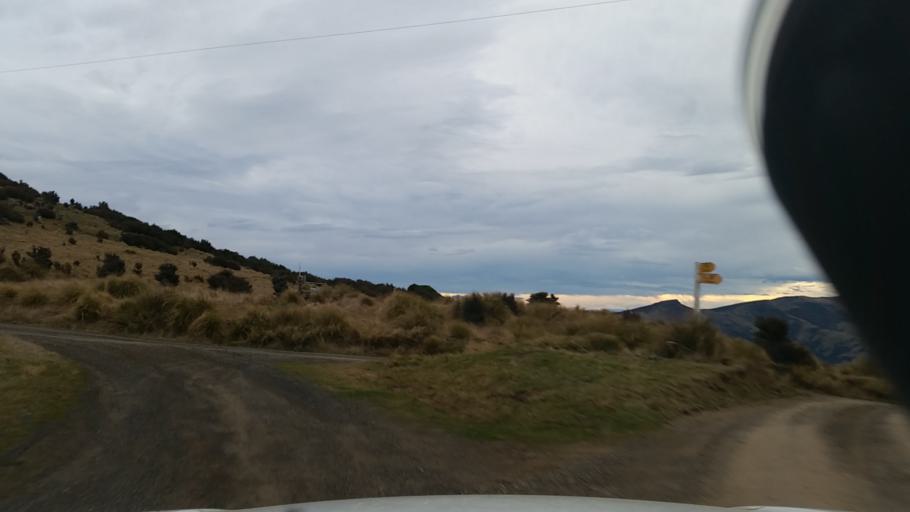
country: NZ
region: Canterbury
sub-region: Christchurch City
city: Christchurch
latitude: -43.8496
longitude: 172.9715
